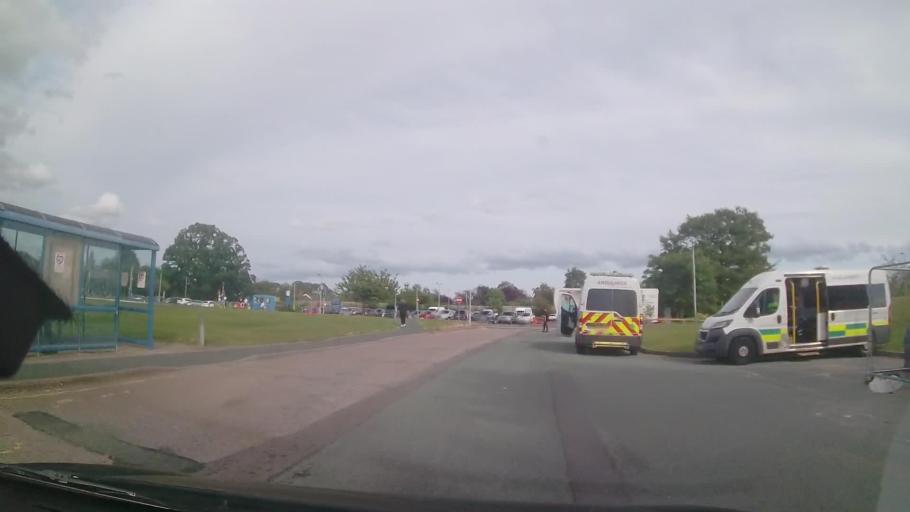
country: GB
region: England
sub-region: Shropshire
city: Bicton
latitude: 52.7084
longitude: -2.7924
